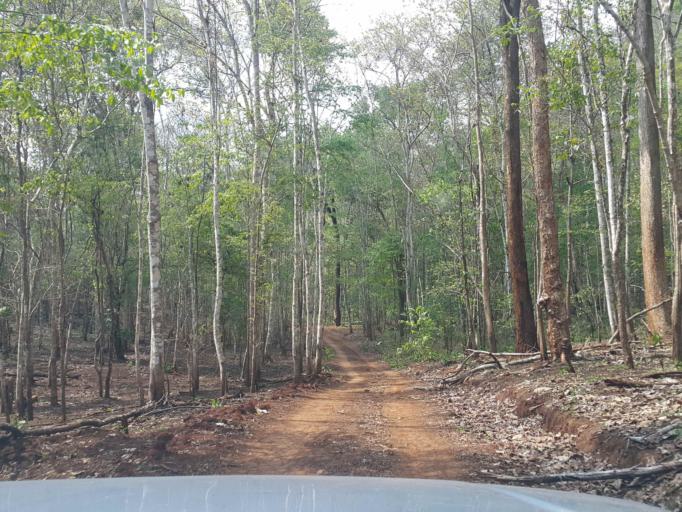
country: TH
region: Chiang Mai
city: Wiang Haeng
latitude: 19.3342
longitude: 98.7184
